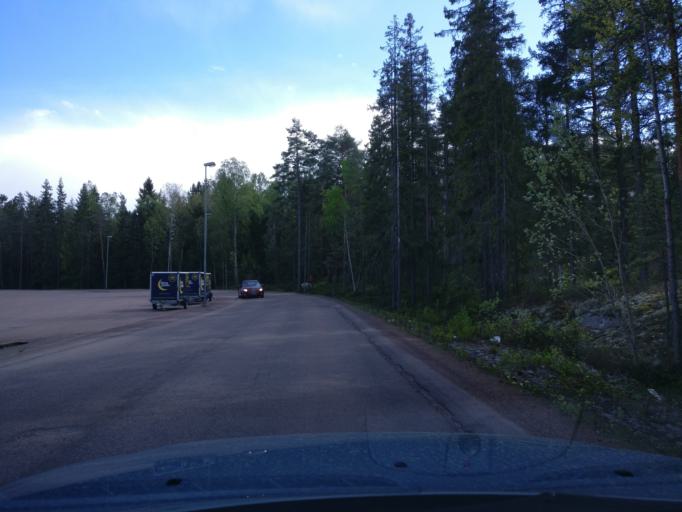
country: SE
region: Vaermland
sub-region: Hammaro Kommun
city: Skoghall
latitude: 59.3753
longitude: 13.4381
